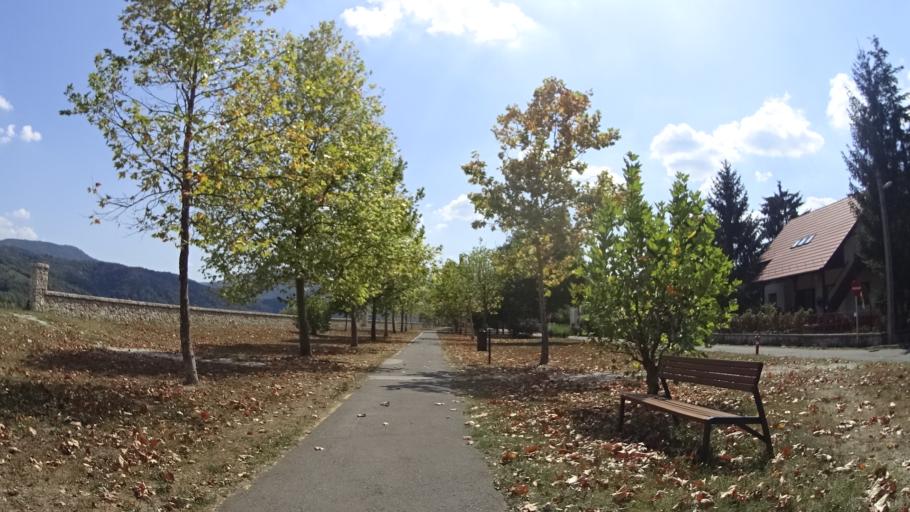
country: HU
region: Pest
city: Nagymaros
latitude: 47.7813
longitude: 18.9569
